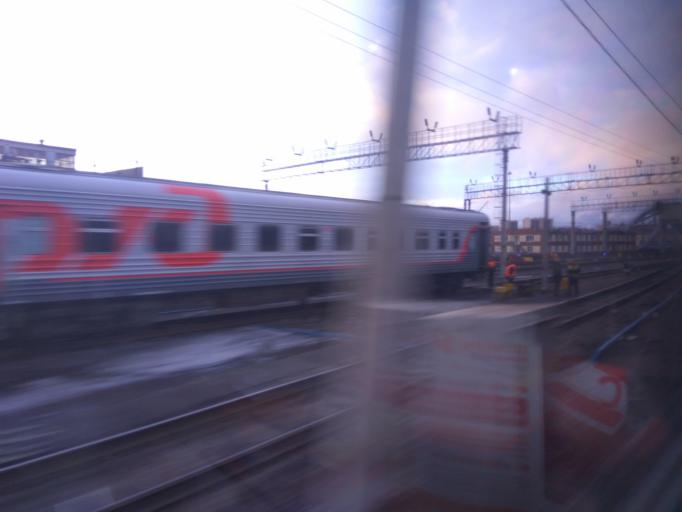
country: RU
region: St.-Petersburg
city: Centralniy
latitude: 59.9116
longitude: 30.3685
